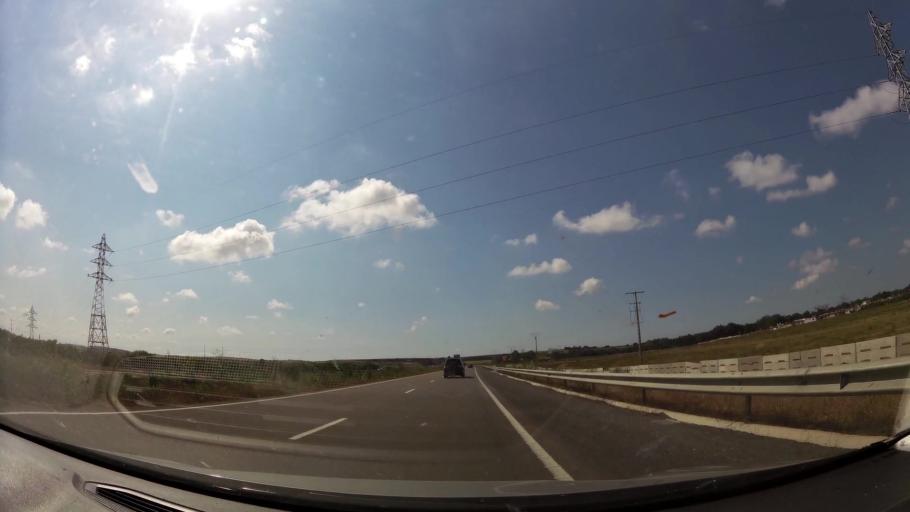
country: MA
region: Rabat-Sale-Zemmour-Zaer
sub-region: Skhirate-Temara
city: Temara
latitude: 33.8414
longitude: -6.8859
